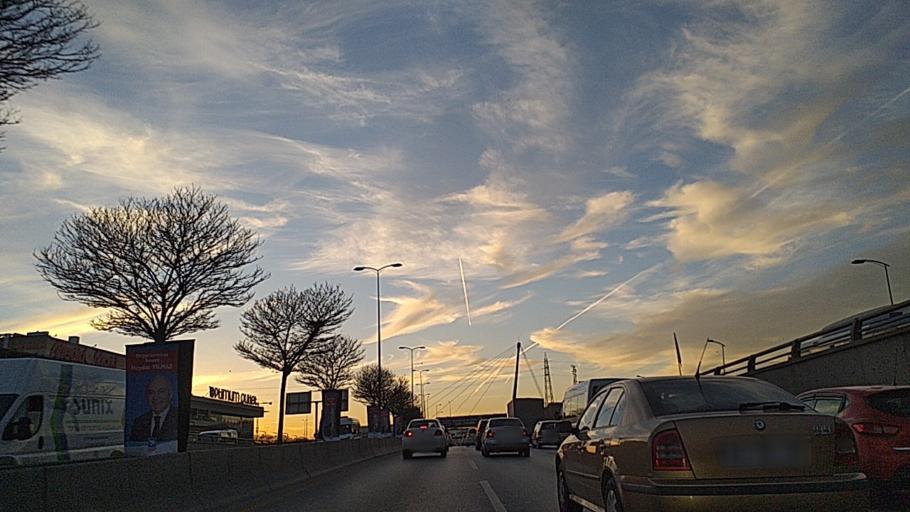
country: TR
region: Ankara
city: Etimesgut
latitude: 39.9661
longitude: 32.6341
